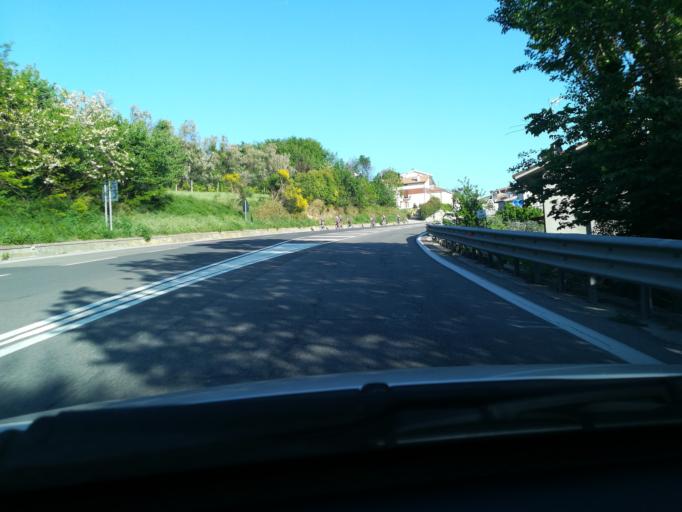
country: IT
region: The Marches
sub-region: Provincia di Pesaro e Urbino
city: Gradara
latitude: 43.9446
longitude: 12.8203
